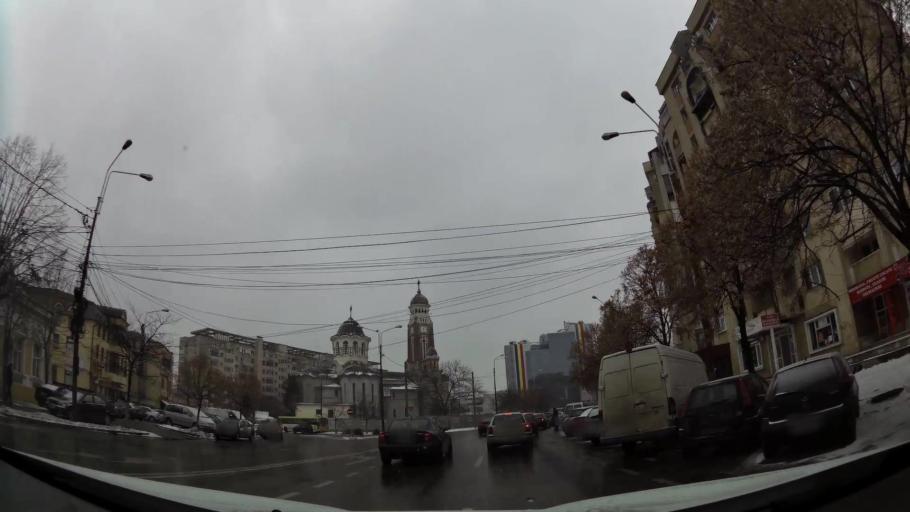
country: RO
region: Prahova
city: Ploiesti
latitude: 44.9445
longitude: 26.0190
